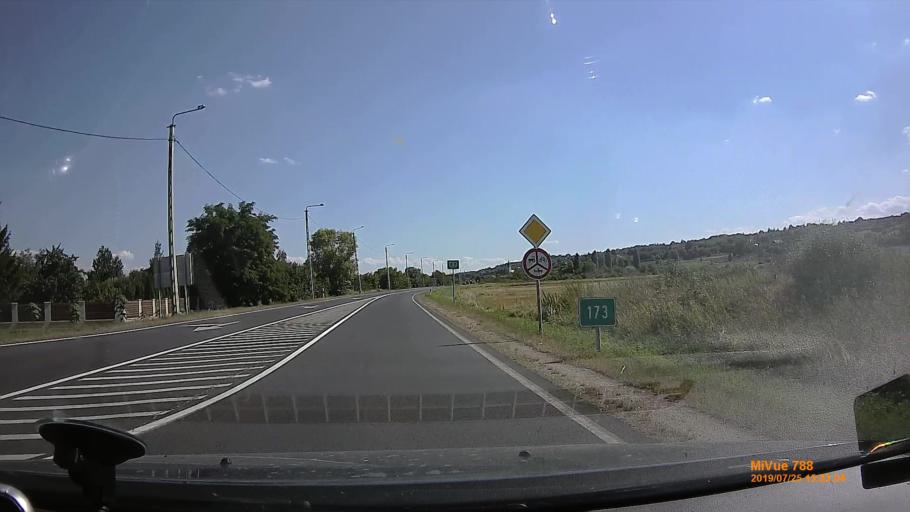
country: HU
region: Borsod-Abauj-Zemplen
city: Nyekladhaza
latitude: 47.9998
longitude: 20.8315
